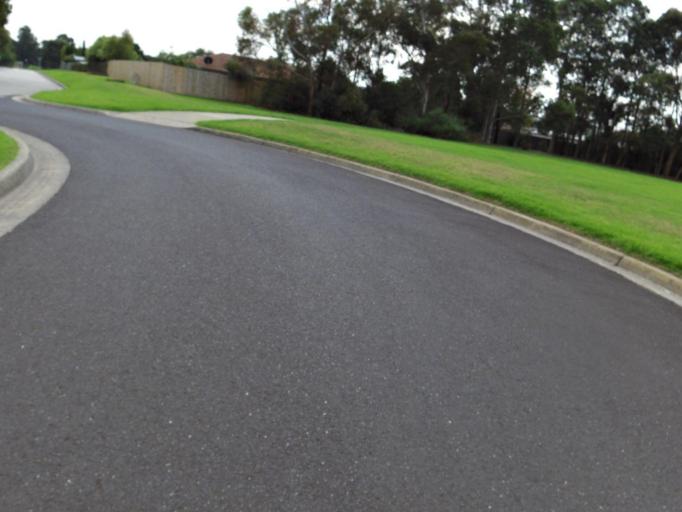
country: AU
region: Victoria
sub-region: Casey
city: Berwick
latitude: -38.0251
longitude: 145.3263
